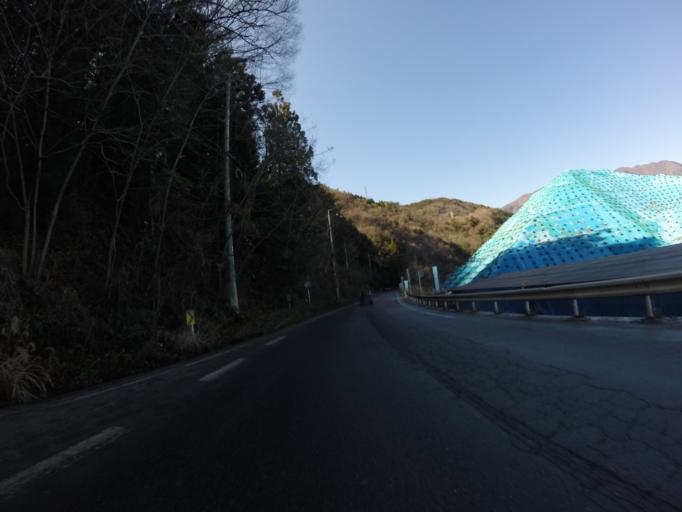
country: JP
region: Yamanashi
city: Ryuo
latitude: 35.4270
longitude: 138.4303
